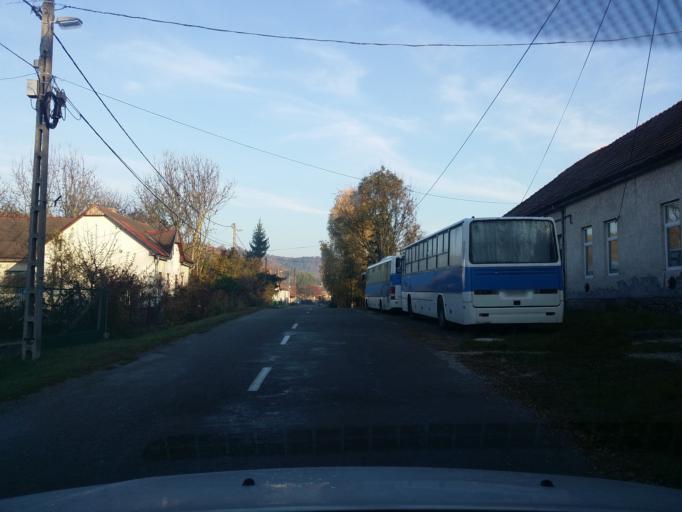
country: HU
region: Borsod-Abauj-Zemplen
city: Borsodnadasd
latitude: 48.0509
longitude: 20.2696
